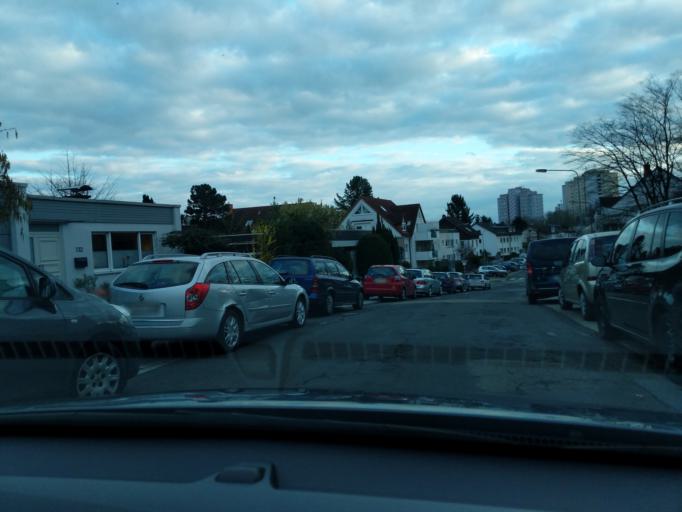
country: DE
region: Hesse
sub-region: Regierungsbezirk Darmstadt
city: Bad Vilbel
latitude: 50.1459
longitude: 8.7211
